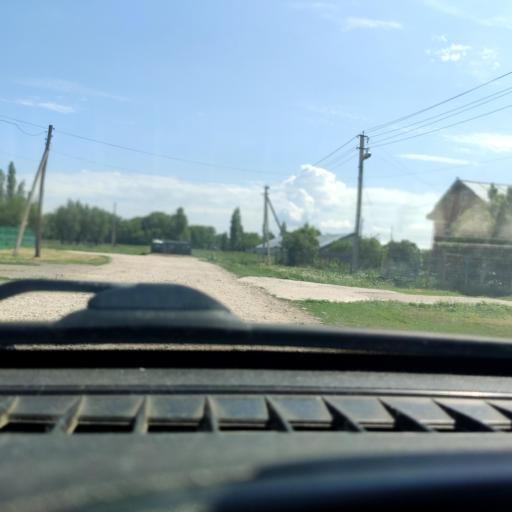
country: RU
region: Samara
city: Tol'yatti
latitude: 53.6354
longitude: 49.2970
